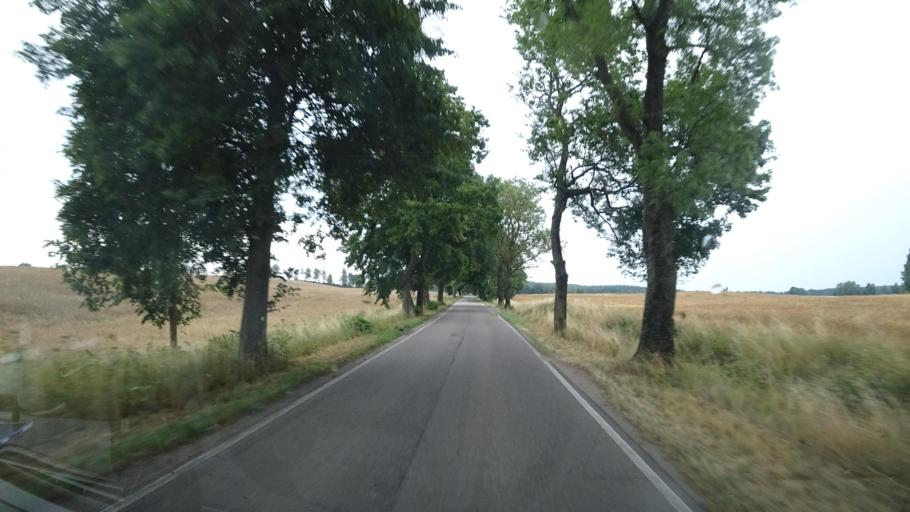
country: PL
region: Warmian-Masurian Voivodeship
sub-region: Powiat gizycki
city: Ryn
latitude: 53.9039
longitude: 21.5648
